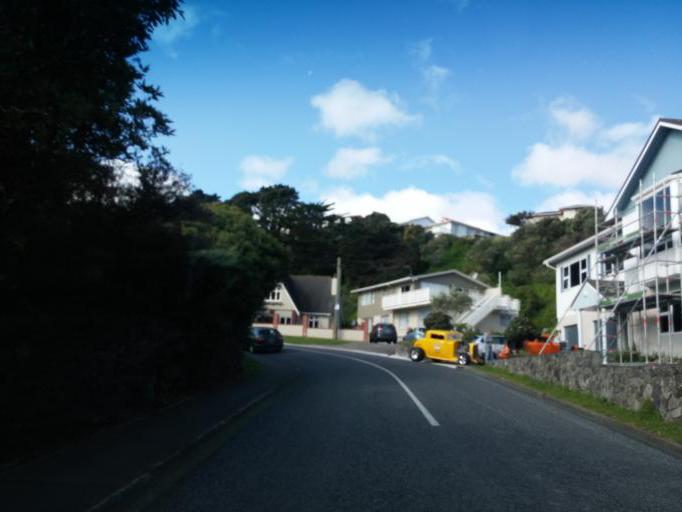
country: NZ
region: Wellington
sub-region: Wellington City
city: Wellington
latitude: -41.3215
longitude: 174.8208
